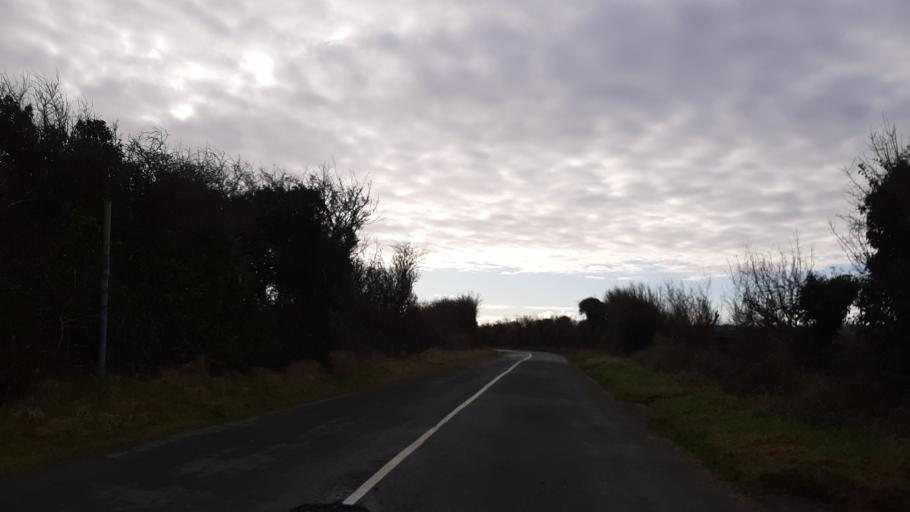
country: IE
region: Connaught
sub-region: County Galway
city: Gaillimh
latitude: 53.3150
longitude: -9.0660
